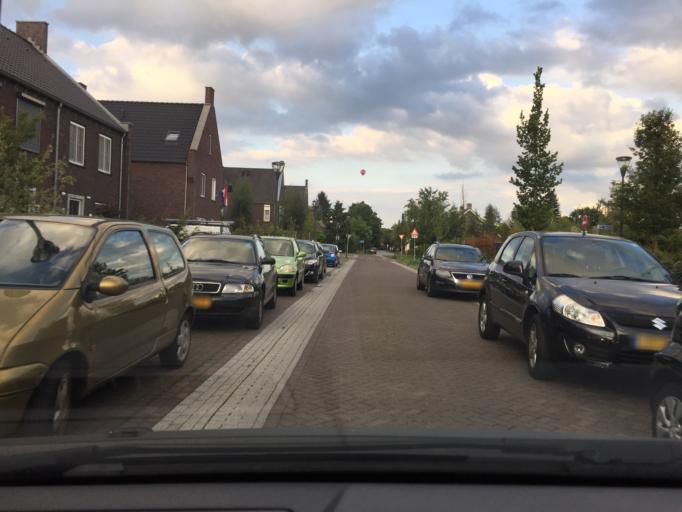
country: NL
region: North Brabant
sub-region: Gemeente Laarbeek
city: Aarle-Rixtel
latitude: 51.5254
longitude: 5.6370
